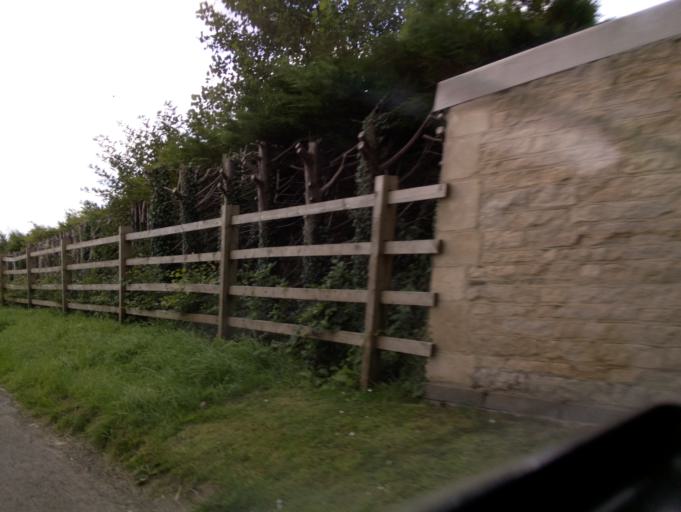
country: GB
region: England
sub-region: Gloucestershire
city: Chalford
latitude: 51.7635
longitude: -2.0881
